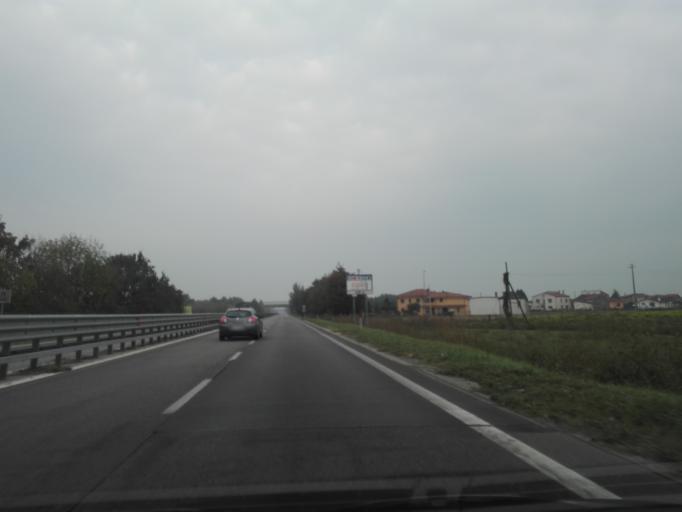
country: IT
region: Veneto
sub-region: Provincia di Verona
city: Spinimbecco
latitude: 45.1357
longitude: 11.3643
